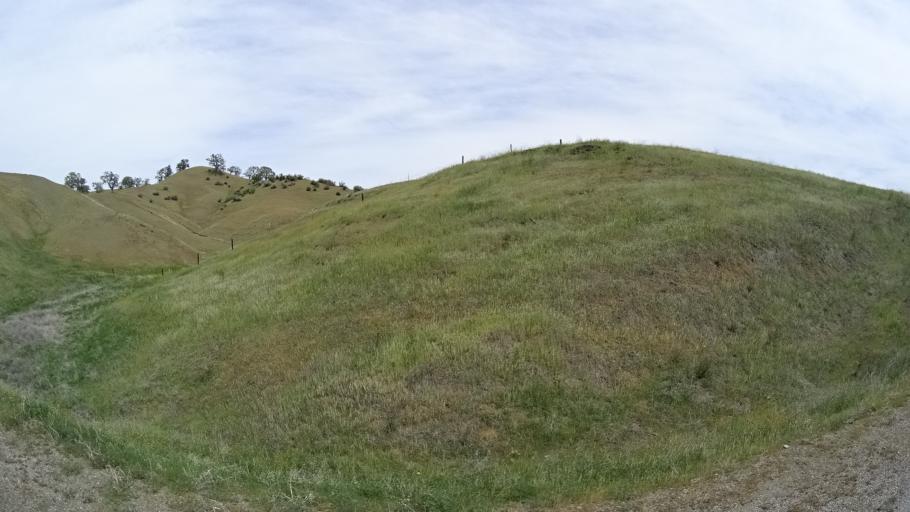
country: US
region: California
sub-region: Glenn County
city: Willows
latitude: 39.6178
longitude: -122.5916
